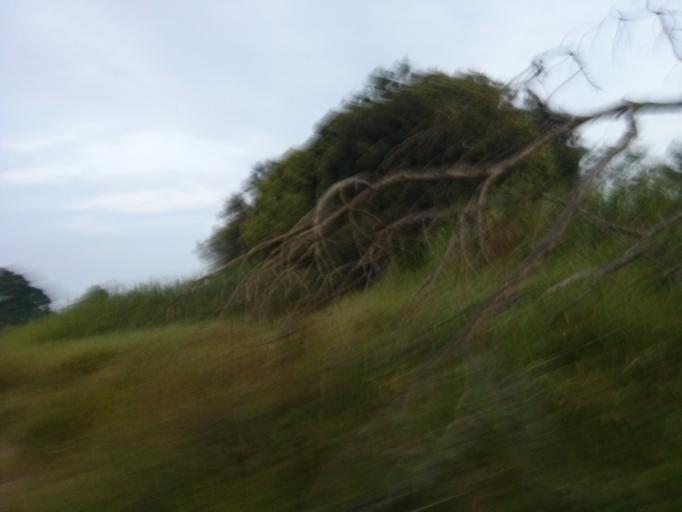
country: MY
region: Johor
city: Johor Bahru
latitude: 1.3845
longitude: 103.6866
